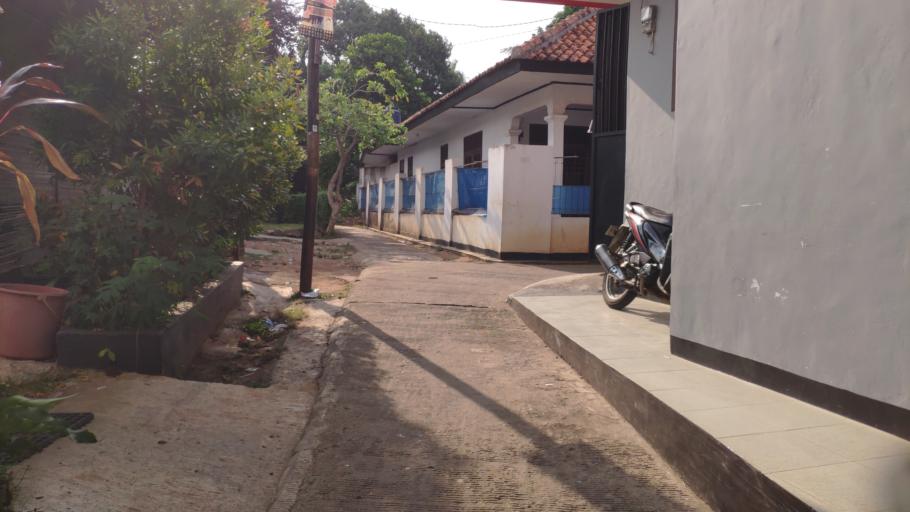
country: ID
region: West Java
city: Pamulang
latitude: -6.2991
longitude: 106.8018
